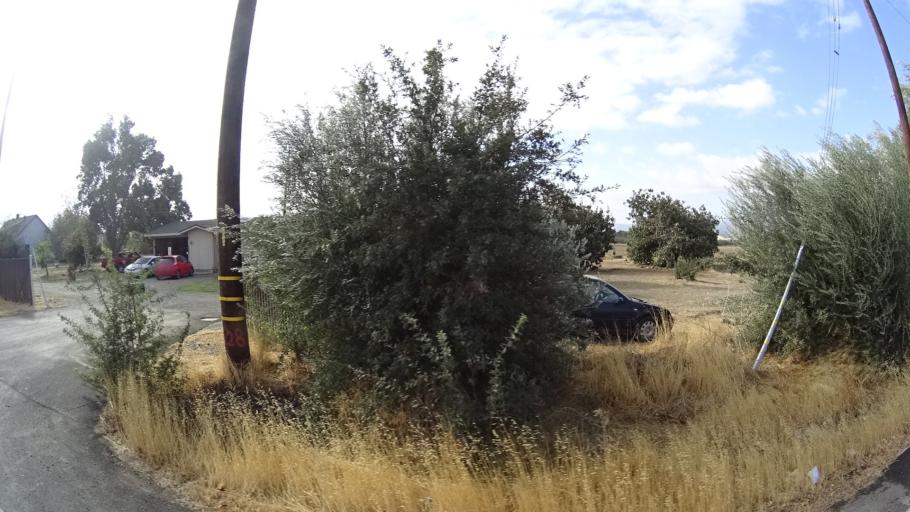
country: US
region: California
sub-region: Yolo County
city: Esparto
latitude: 38.6892
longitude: -122.0185
